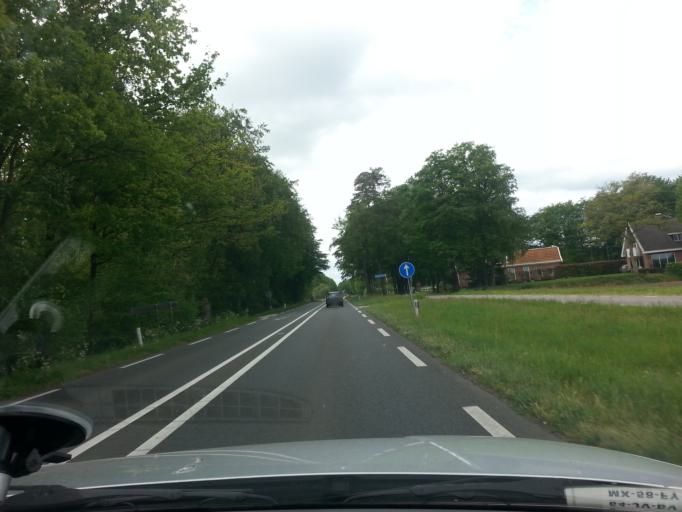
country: NL
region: Overijssel
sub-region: Gemeente Oldenzaal
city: Oldenzaal
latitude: 52.3468
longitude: 6.9709
